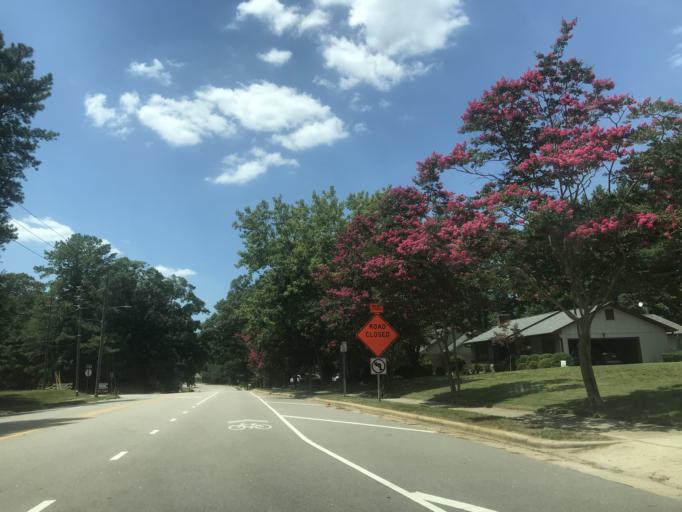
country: US
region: North Carolina
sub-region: Wake County
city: Cary
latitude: 35.7808
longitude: -78.7749
